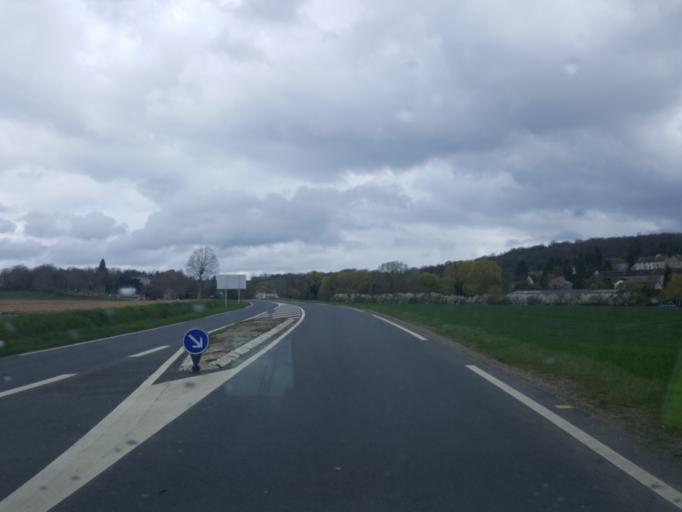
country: FR
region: Ile-de-France
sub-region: Departement du Val-d'Oise
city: Magny-en-Vexin
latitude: 49.1595
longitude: 1.7834
